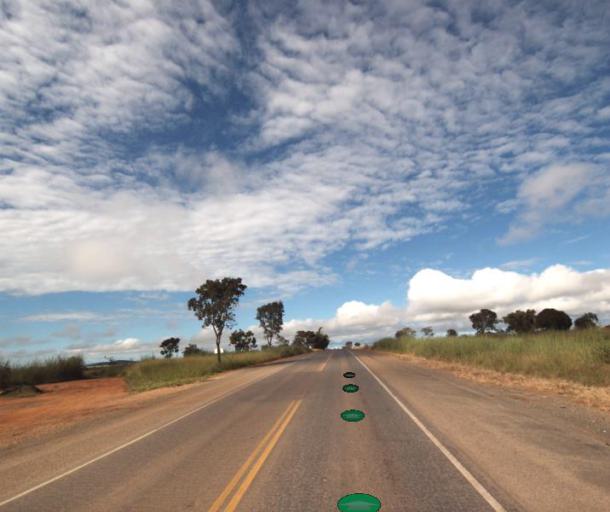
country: BR
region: Goias
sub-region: Uruacu
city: Uruacu
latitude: -14.6955
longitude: -49.2155
